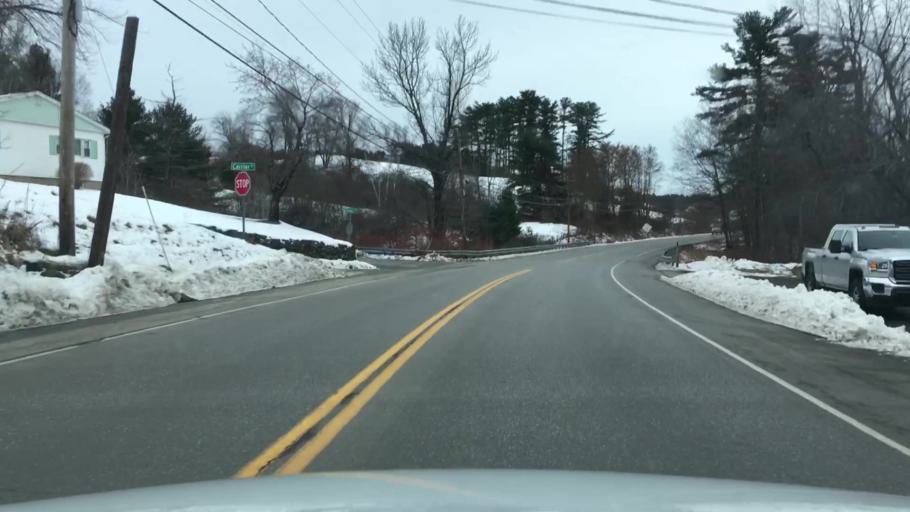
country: US
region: Maine
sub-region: Androscoggin County
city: Lewiston
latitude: 44.0645
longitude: -70.2085
